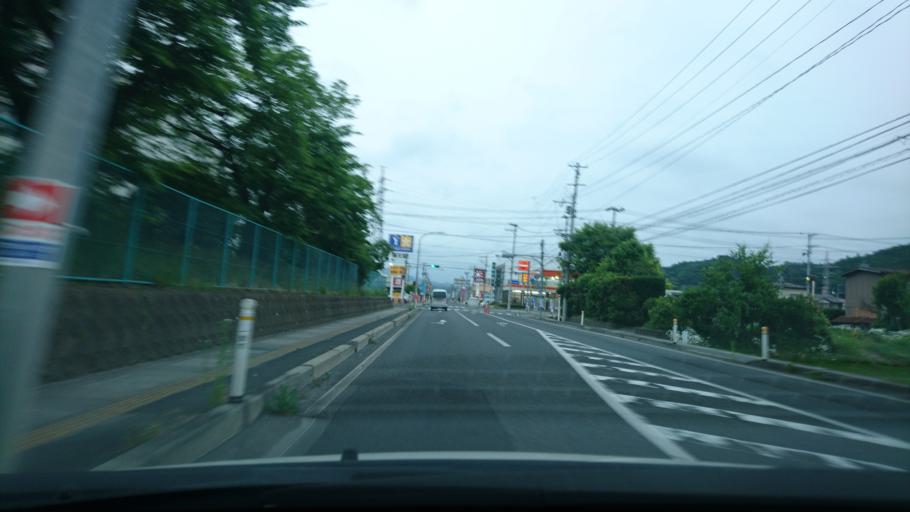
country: JP
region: Iwate
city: Ichinoseki
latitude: 38.9240
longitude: 141.1435
